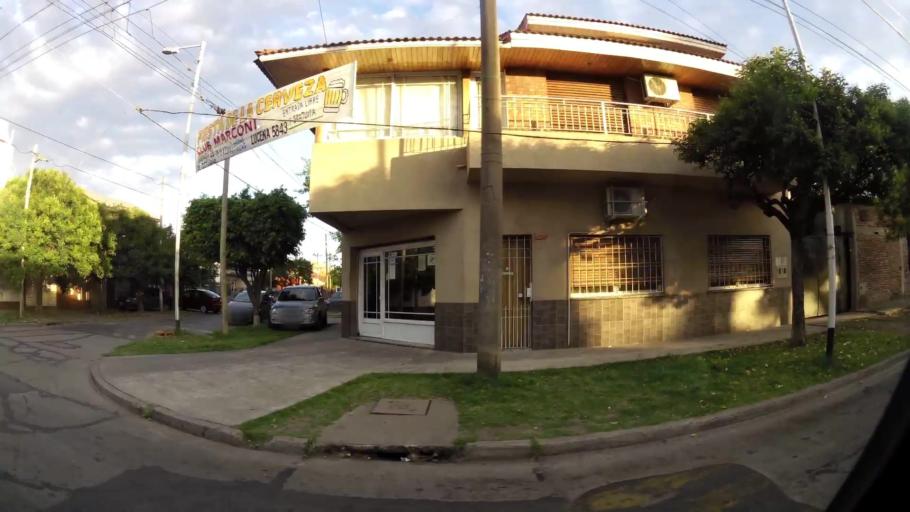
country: AR
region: Buenos Aires
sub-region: Partido de Avellaneda
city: Avellaneda
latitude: -34.7107
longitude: -58.3335
